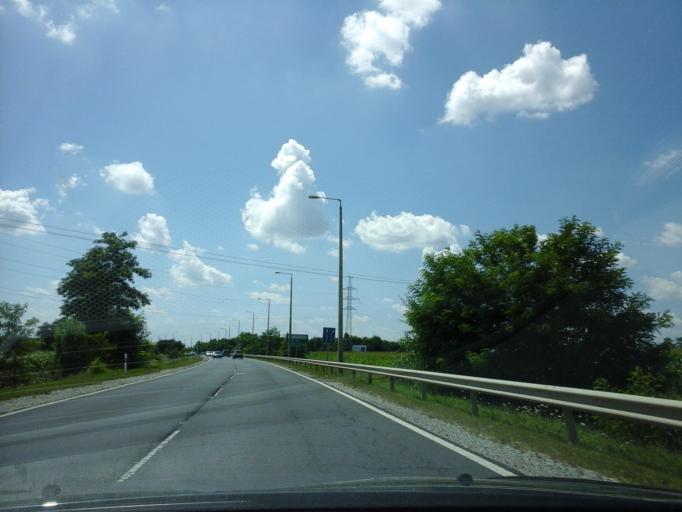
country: HU
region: Hajdu-Bihar
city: Ebes
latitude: 47.4631
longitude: 21.4504
